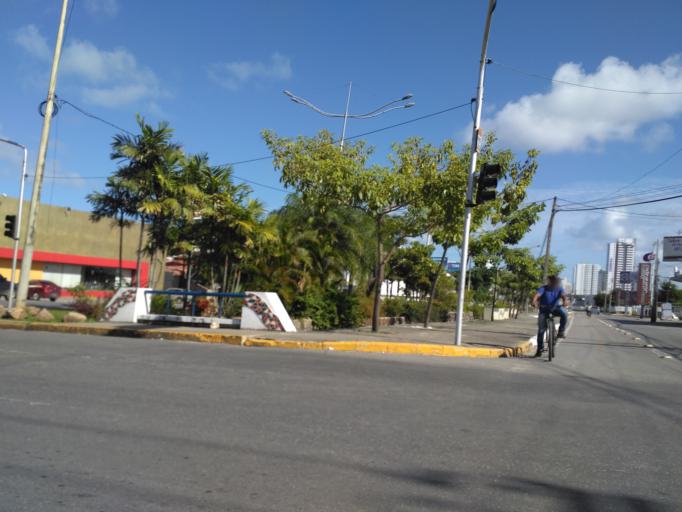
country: BR
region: Pernambuco
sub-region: Jaboatao Dos Guararapes
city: Jaboatao
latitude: -8.1658
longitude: -34.9159
